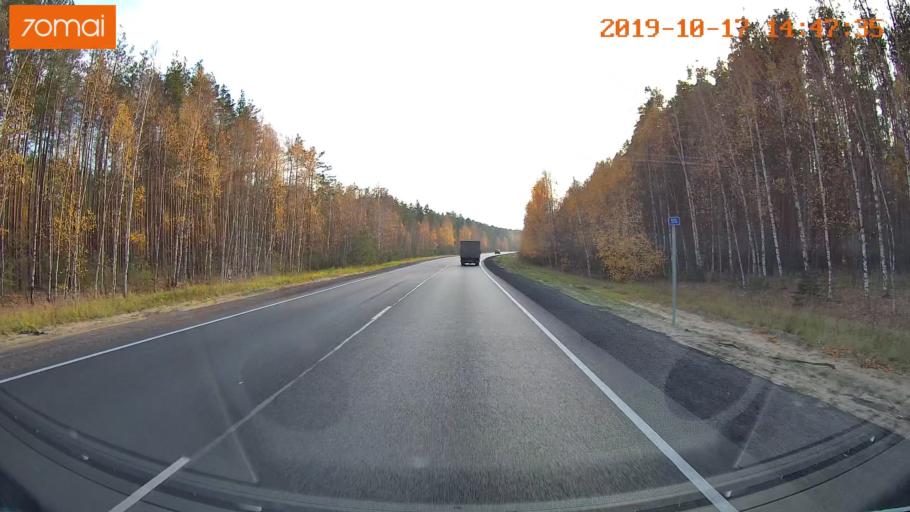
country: RU
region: Rjazan
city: Solotcha
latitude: 54.7694
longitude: 39.8593
